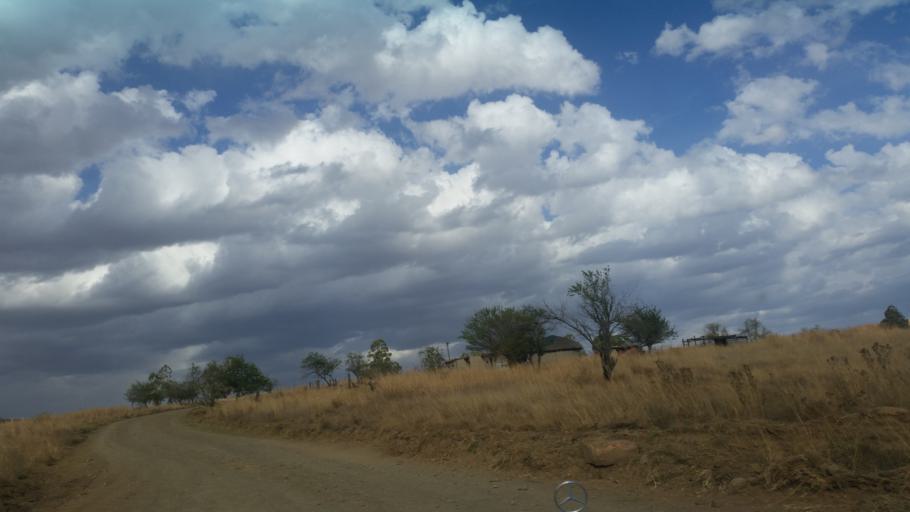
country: ZA
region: Orange Free State
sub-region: Thabo Mofutsanyana District Municipality
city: Phuthaditjhaba
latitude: -28.3710
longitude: 28.5968
